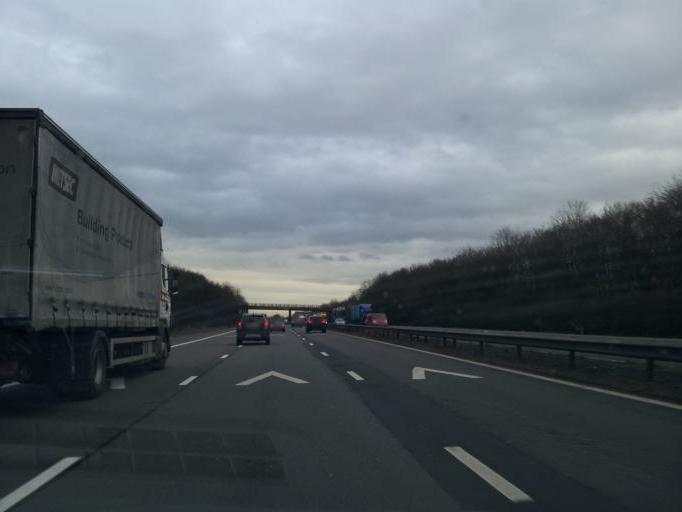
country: GB
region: England
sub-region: Warwickshire
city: Long Lawford
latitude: 52.4248
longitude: -1.3124
